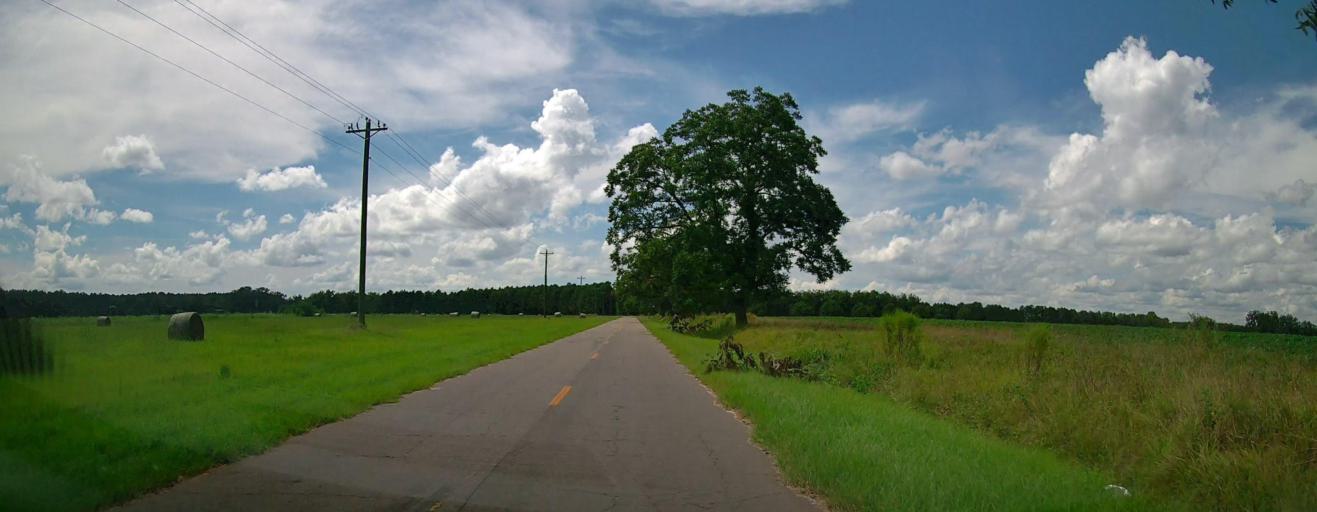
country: US
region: Georgia
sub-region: Macon County
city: Marshallville
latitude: 32.4485
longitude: -83.9940
